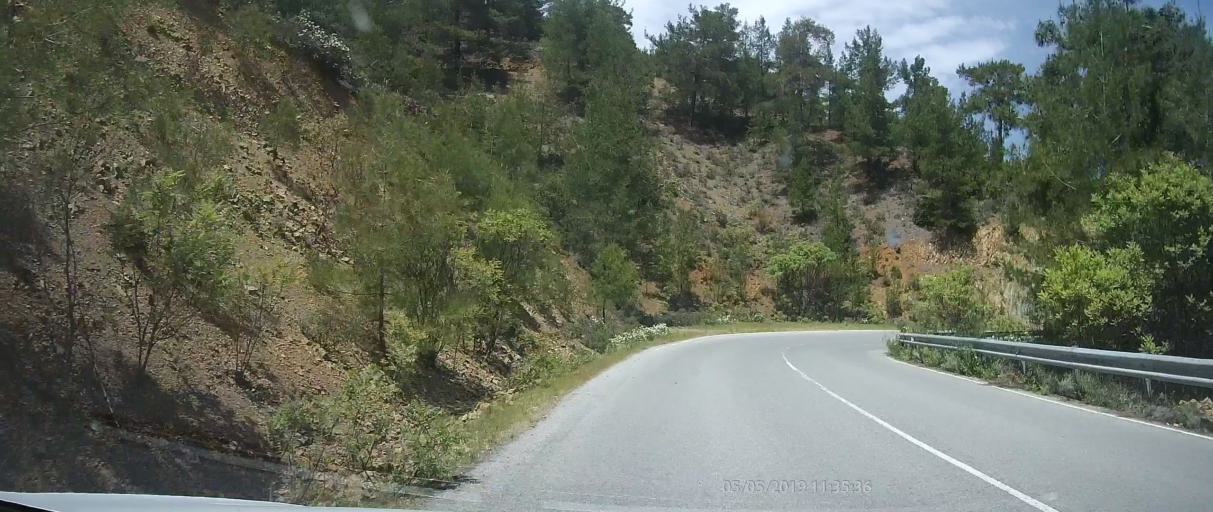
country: CY
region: Lefkosia
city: Kato Pyrgos
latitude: 34.9686
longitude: 32.6519
